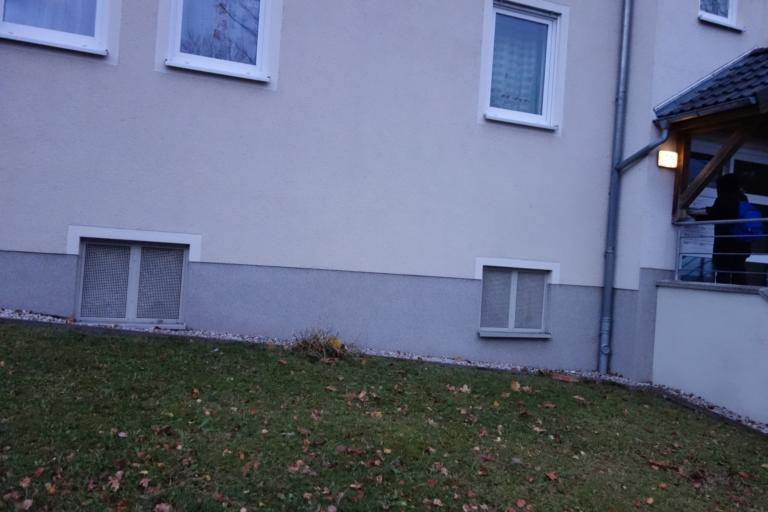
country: DE
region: Saxony
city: Augustusburg
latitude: 50.8170
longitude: 13.1014
